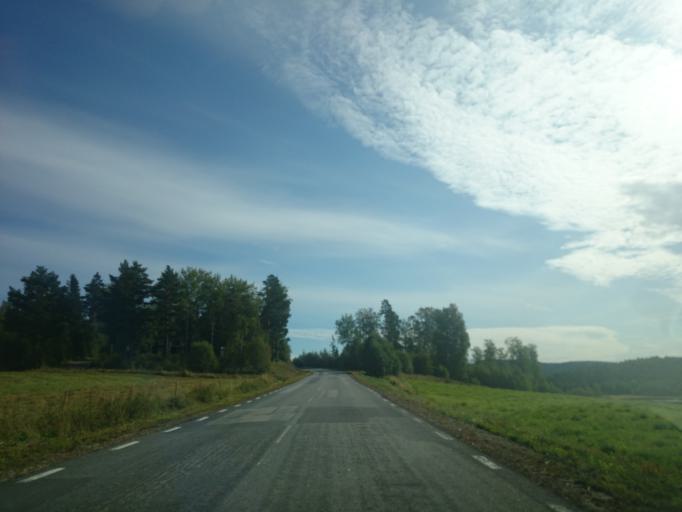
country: SE
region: Vaesternorrland
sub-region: Kramfors Kommun
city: Nordingra
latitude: 62.8850
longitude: 18.1061
